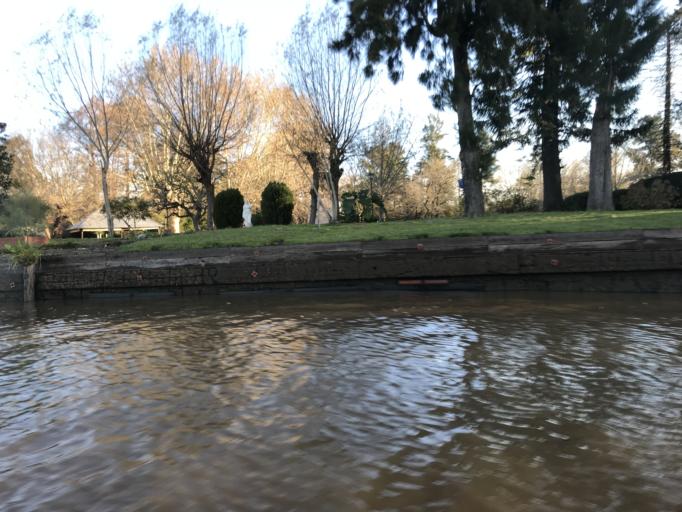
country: AR
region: Buenos Aires
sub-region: Partido de Tigre
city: Tigre
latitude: -34.3895
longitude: -58.5761
